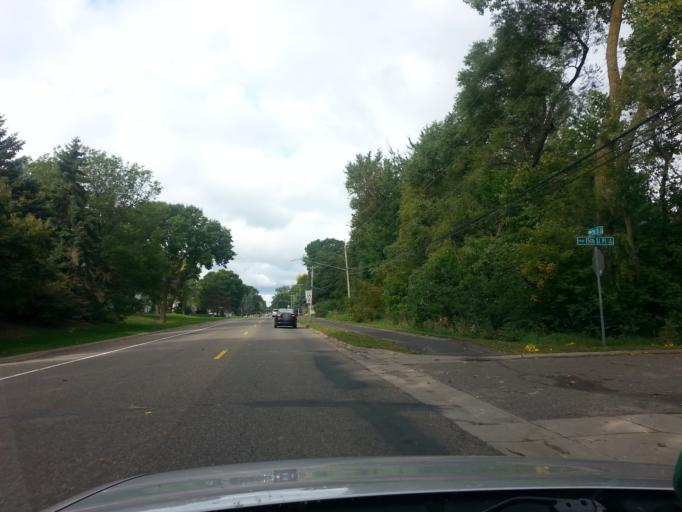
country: US
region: Minnesota
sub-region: Washington County
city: Oakdale
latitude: 44.9705
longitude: -92.9753
